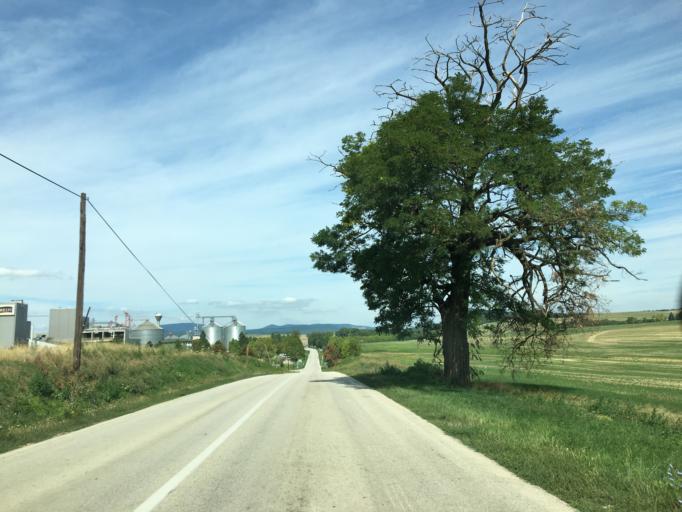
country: HU
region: Fejer
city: Many
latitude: 47.6040
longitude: 18.6491
